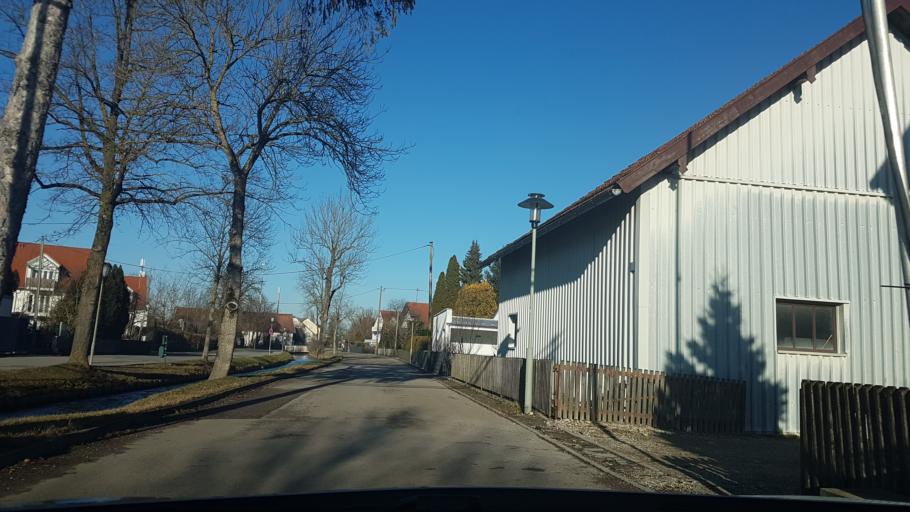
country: DE
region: Bavaria
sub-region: Upper Bavaria
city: Hallbergmoos
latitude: 48.3072
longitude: 11.7456
